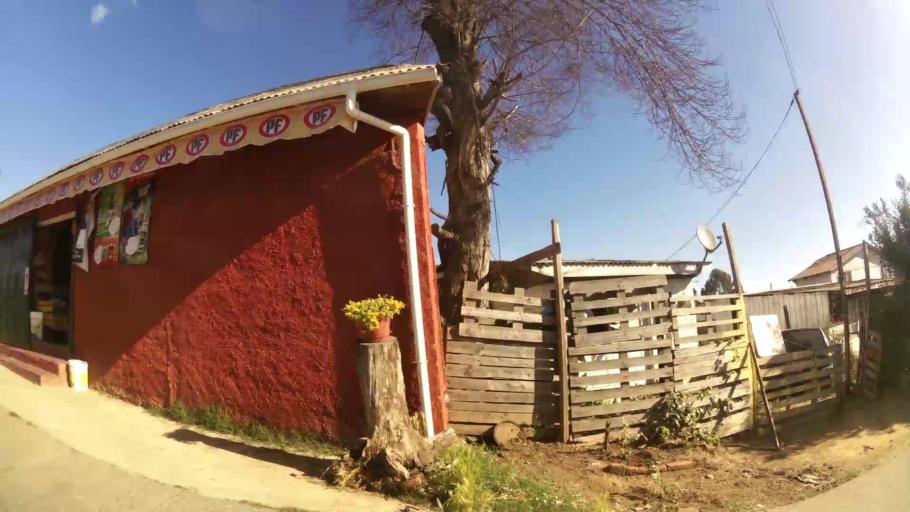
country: CL
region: Valparaiso
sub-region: Provincia de Valparaiso
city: Valparaiso
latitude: -33.1150
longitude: -71.5753
